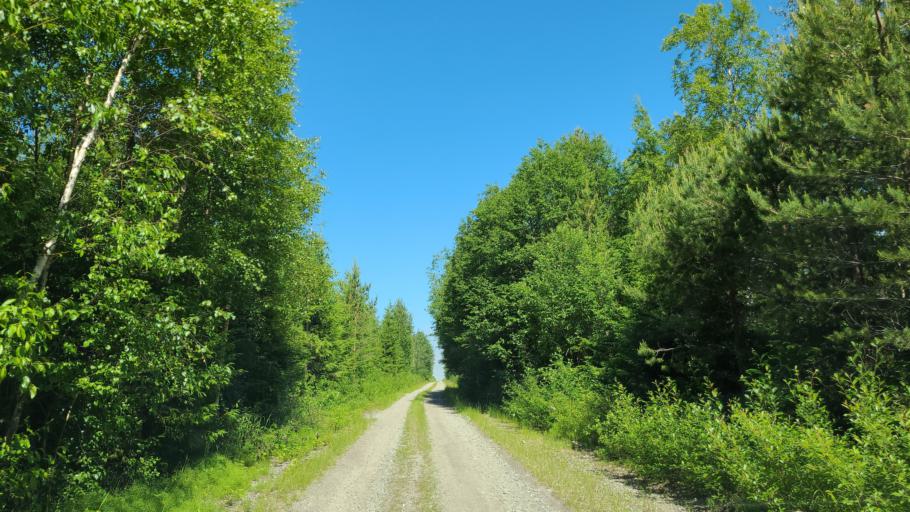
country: SE
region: Vaesternorrland
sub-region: OErnskoeldsviks Kommun
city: Husum
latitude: 63.4352
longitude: 19.2309
